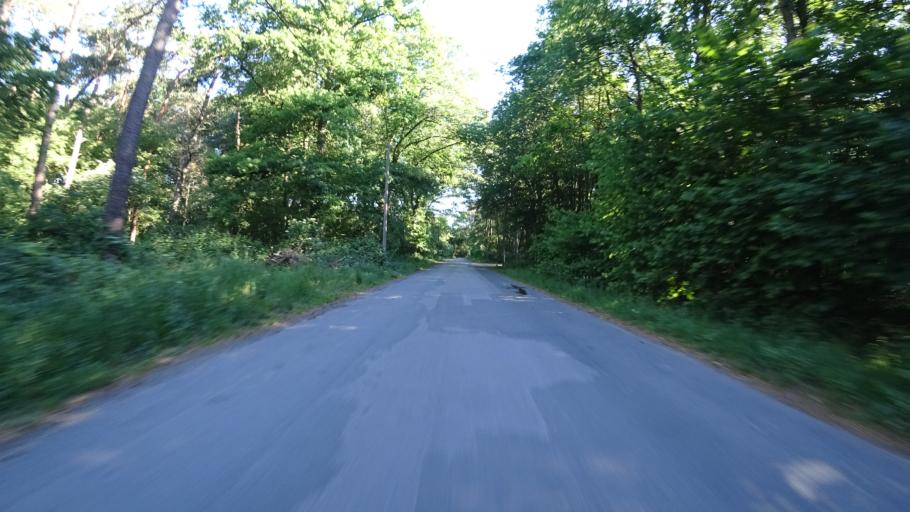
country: DE
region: North Rhine-Westphalia
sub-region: Regierungsbezirk Detmold
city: Rheda-Wiedenbruck
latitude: 51.8714
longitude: 8.3146
